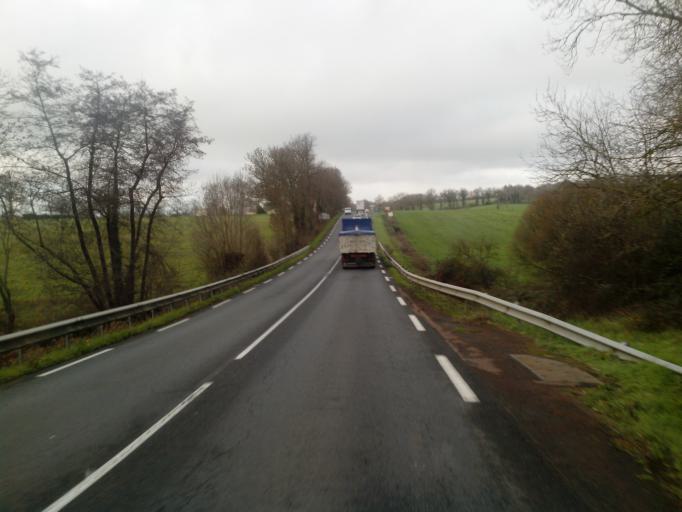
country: FR
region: Poitou-Charentes
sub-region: Departement des Deux-Sevres
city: Chiche
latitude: 46.7407
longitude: -0.3032
